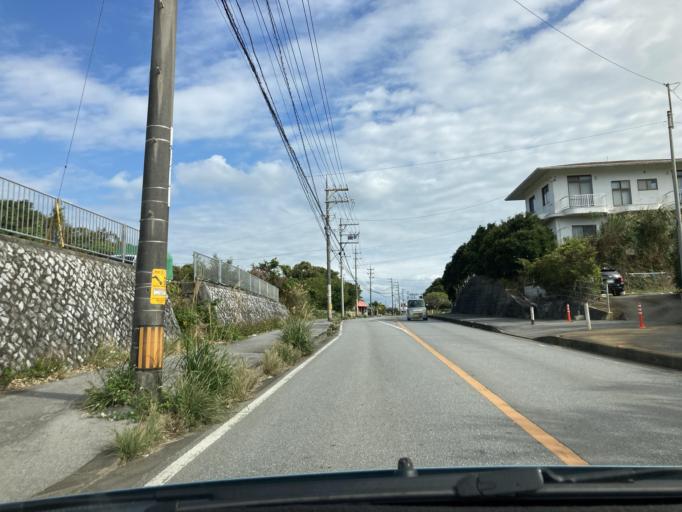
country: JP
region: Okinawa
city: Nago
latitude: 26.6927
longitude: 127.9567
